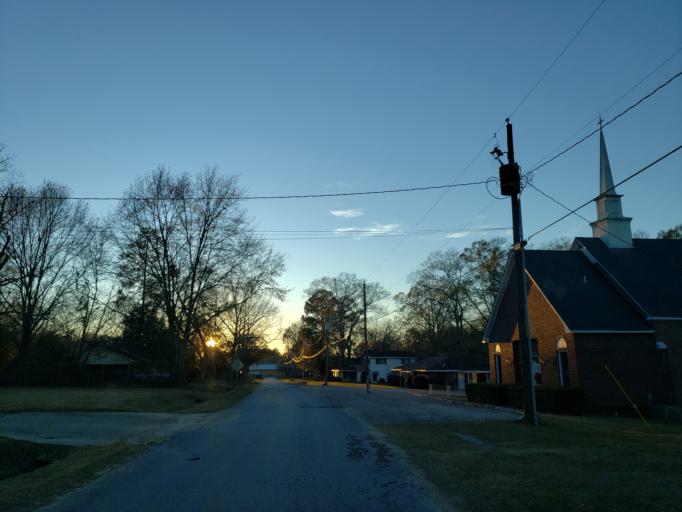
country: US
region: Mississippi
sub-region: Covington County
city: Collins
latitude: 31.5636
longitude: -89.4942
